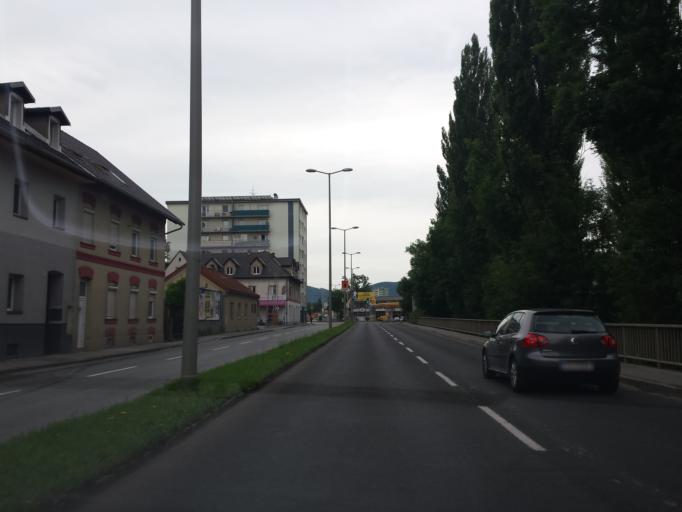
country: AT
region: Styria
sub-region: Graz Stadt
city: Goesting
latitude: 47.0860
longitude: 15.4134
